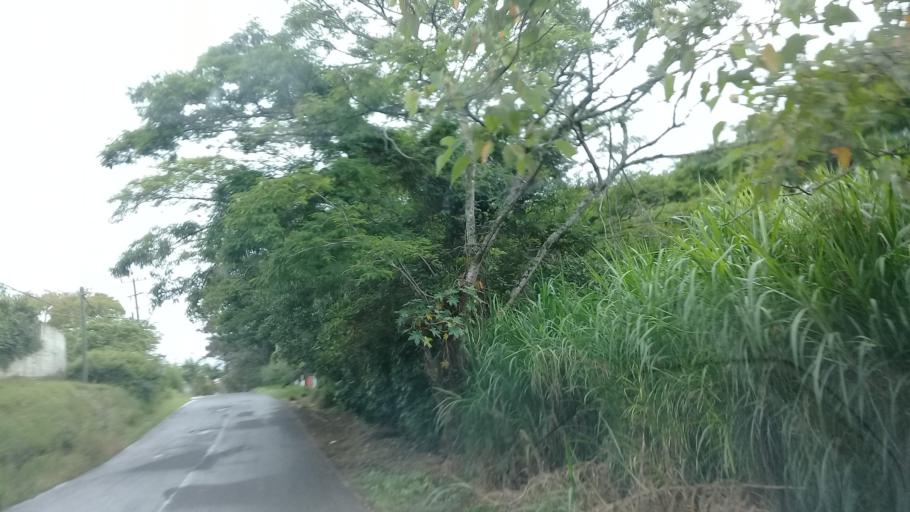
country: MX
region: Veracruz
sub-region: Emiliano Zapata
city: Jacarandas
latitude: 19.5042
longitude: -96.8448
